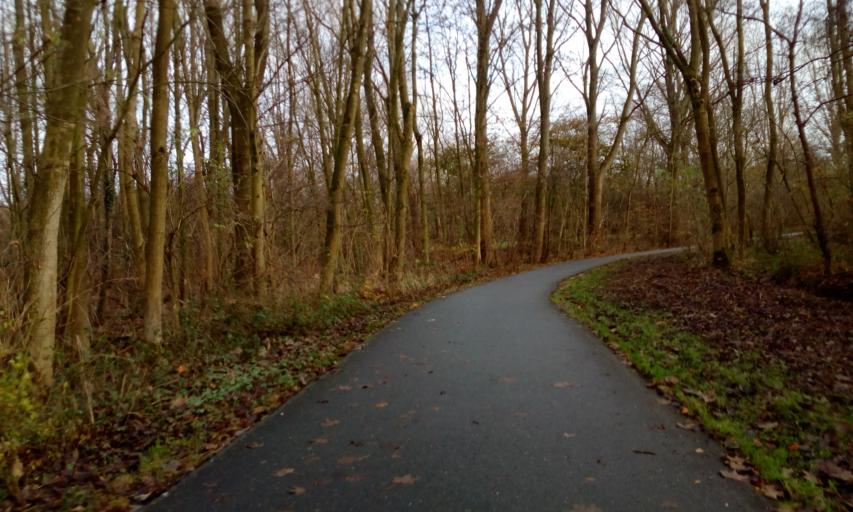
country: NL
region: South Holland
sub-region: Gemeente Lansingerland
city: Bergschenhoek
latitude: 51.9659
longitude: 4.5176
